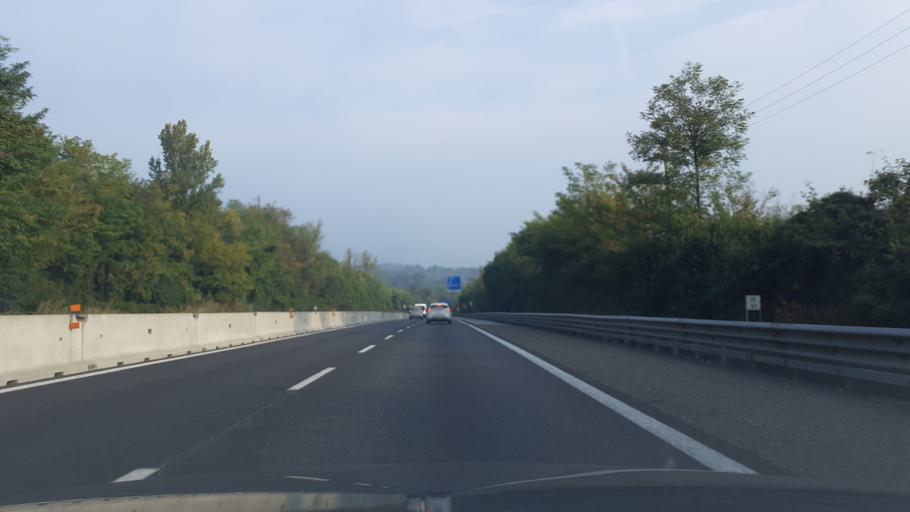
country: IT
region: Lombardy
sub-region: Provincia di Monza e Brianza
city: Briosco
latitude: 45.7109
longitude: 9.2278
